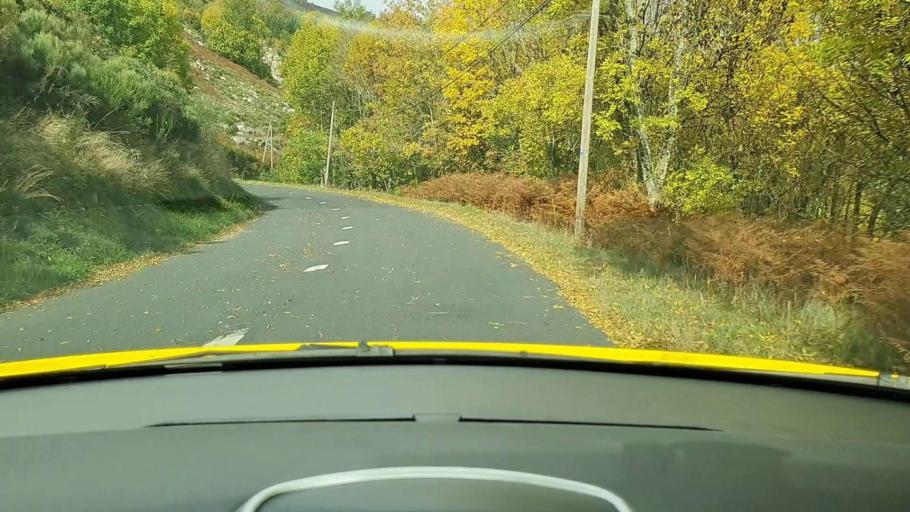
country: FR
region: Languedoc-Roussillon
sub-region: Departement de la Lozere
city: Meyrueis
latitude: 44.0711
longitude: 3.4651
